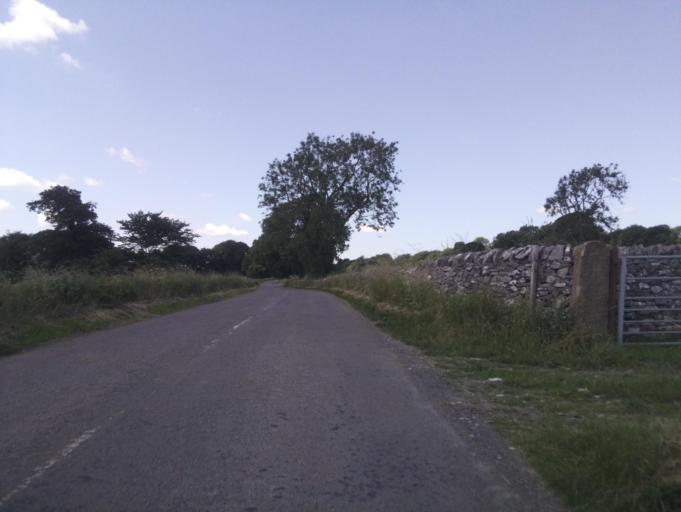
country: GB
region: England
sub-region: Derbyshire
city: Tideswell
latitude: 53.2605
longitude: -1.8067
